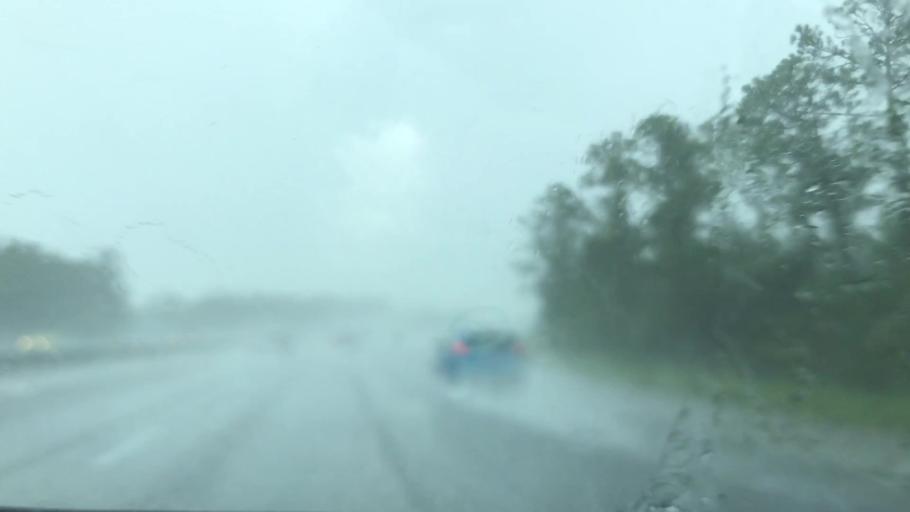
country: US
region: Florida
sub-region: Volusia County
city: Ormond-by-the-Sea
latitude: 29.3489
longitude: -81.1315
